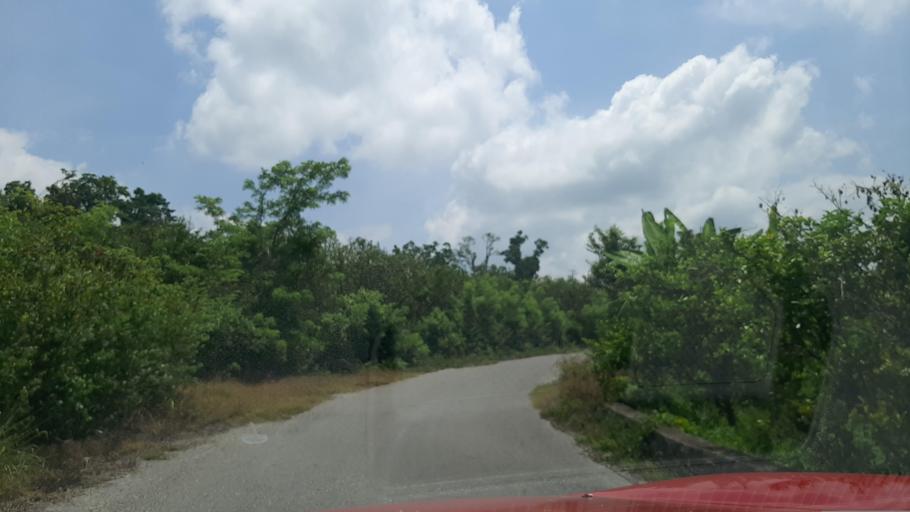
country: MX
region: Veracruz
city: Agua Dulce
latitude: 20.4058
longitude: -97.2836
